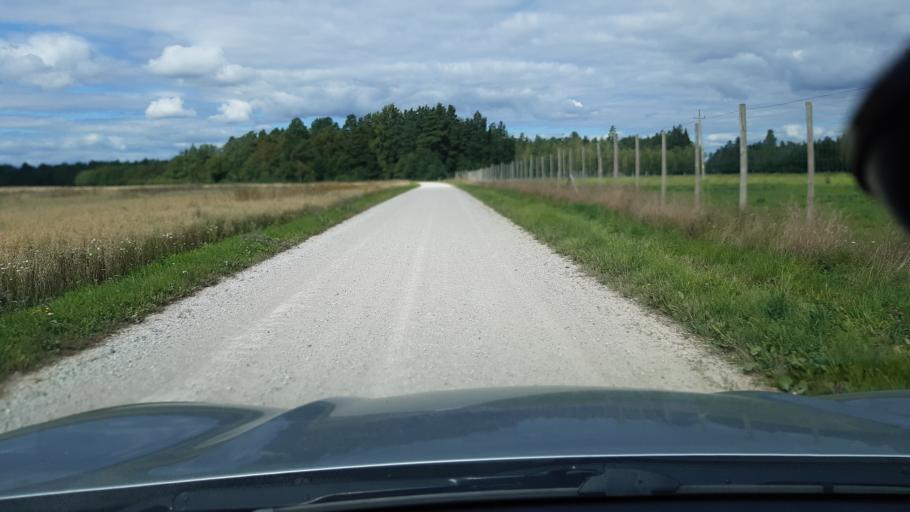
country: EE
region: Paernumaa
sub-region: Vaendra vald (alev)
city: Vandra
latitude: 58.7805
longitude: 25.0501
